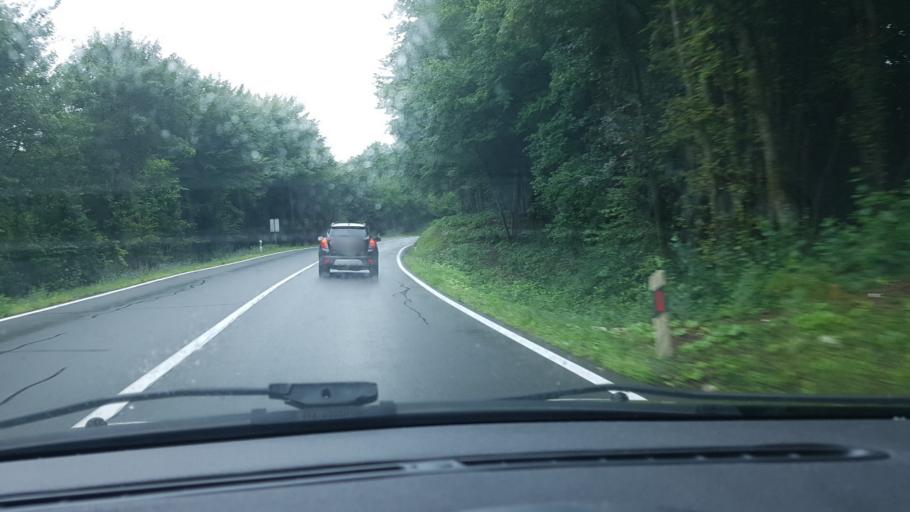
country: HR
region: Karlovacka
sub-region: Grad Karlovac
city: Karlovac
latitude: 45.4547
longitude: 15.4207
